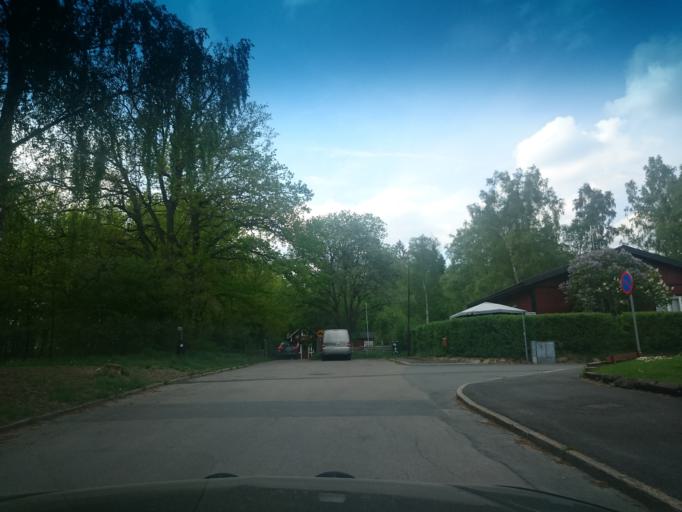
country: SE
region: Joenkoeping
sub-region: Vetlanda Kommun
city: Vetlanda
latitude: 57.4322
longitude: 15.0679
